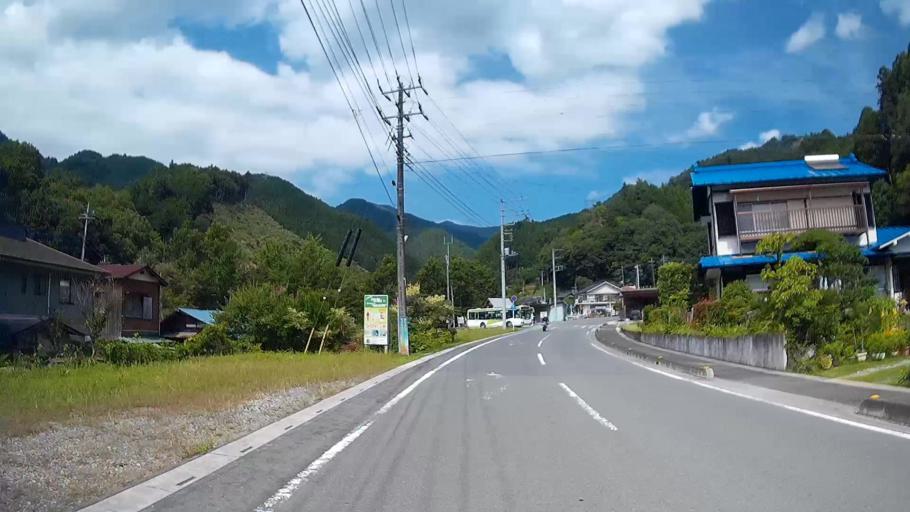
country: JP
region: Saitama
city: Chichibu
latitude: 35.9105
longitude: 139.1492
